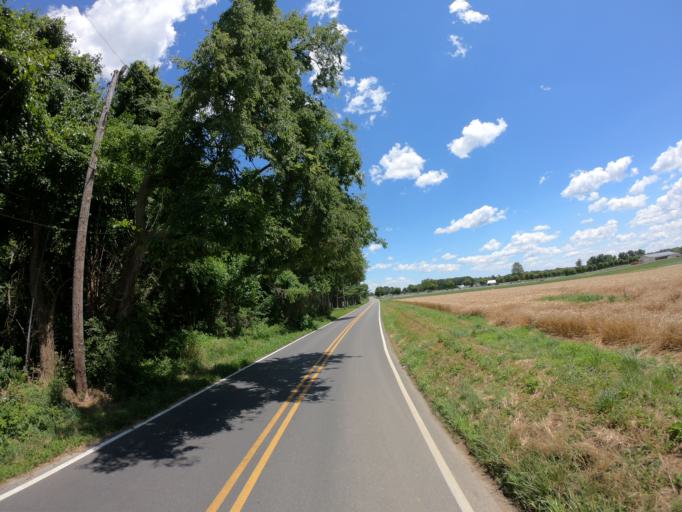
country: US
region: Delaware
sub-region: New Castle County
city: Middletown
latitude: 39.4655
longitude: -75.7680
